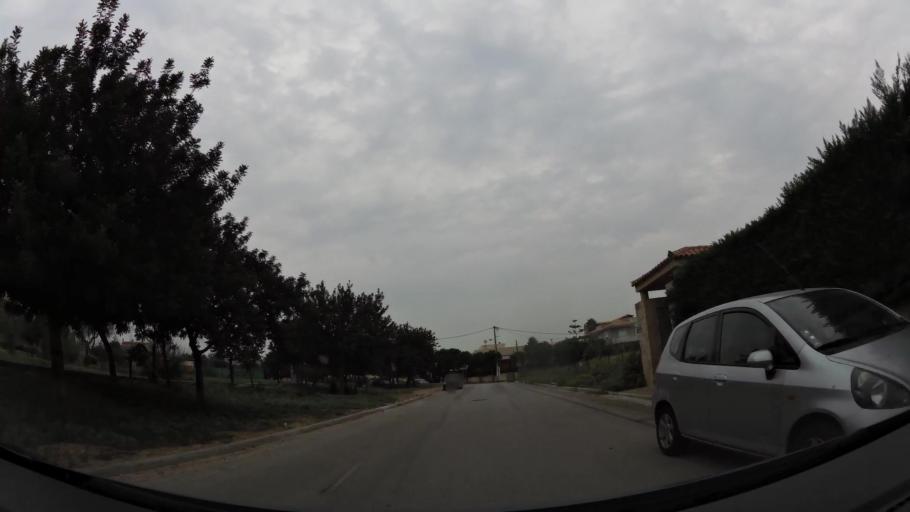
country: GR
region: Attica
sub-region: Nomarchia Athinas
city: Alimos
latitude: 37.9090
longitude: 23.7313
